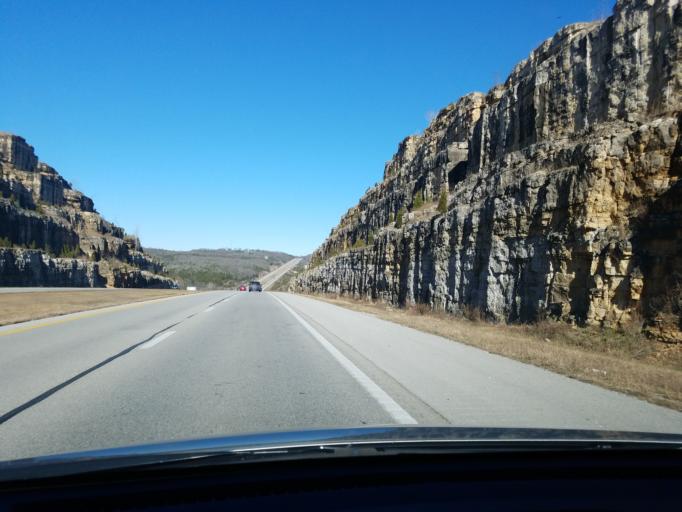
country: US
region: Missouri
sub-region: Taney County
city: Merriam Woods
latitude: 36.7617
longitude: -93.2226
